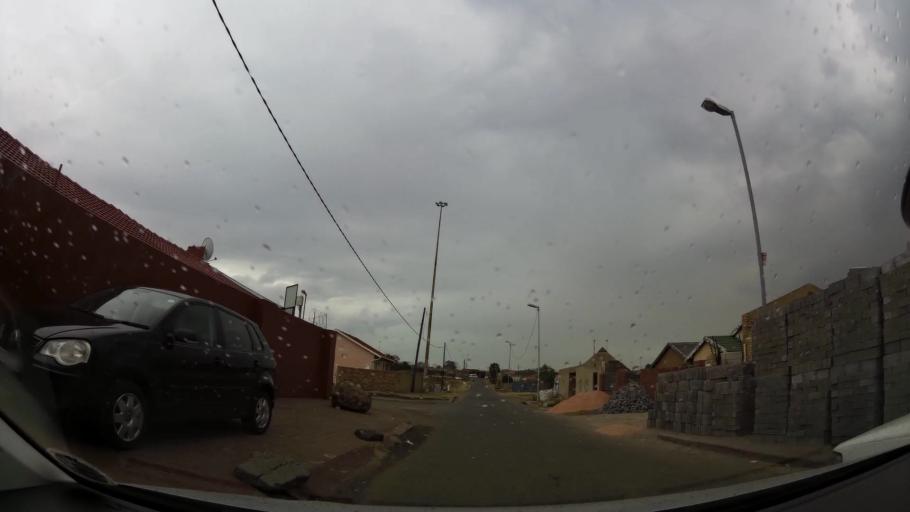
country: ZA
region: Gauteng
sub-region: City of Johannesburg Metropolitan Municipality
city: Soweto
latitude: -26.2592
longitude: 27.8715
